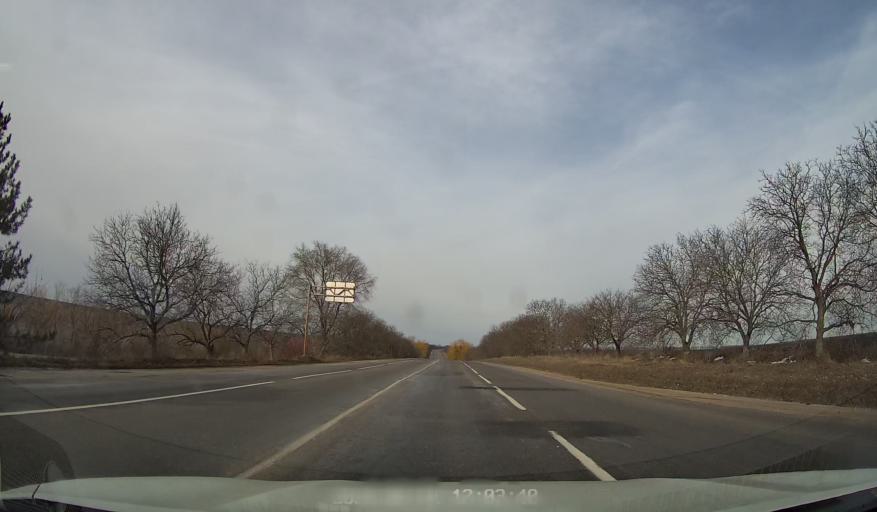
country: MD
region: Riscani
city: Riscani
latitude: 47.9612
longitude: 27.6063
